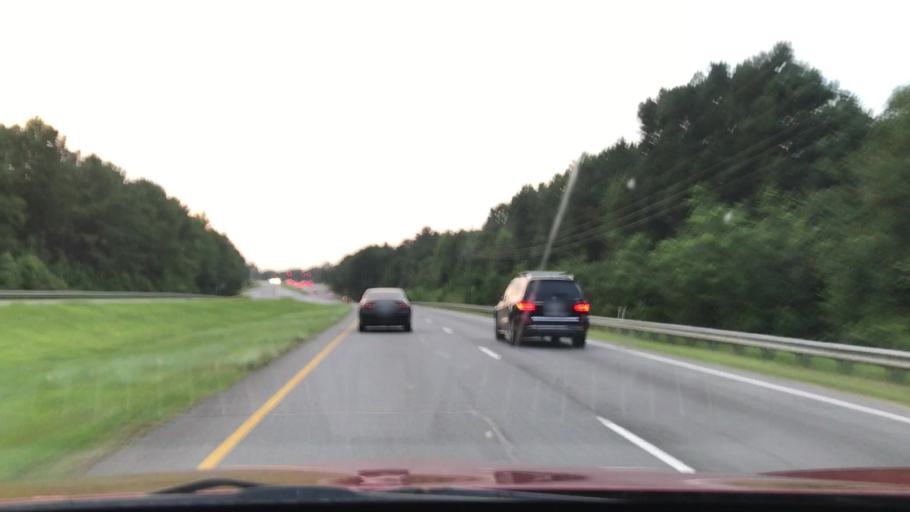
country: US
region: Georgia
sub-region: Gwinnett County
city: Lawrenceville
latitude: 34.0308
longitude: -83.9864
